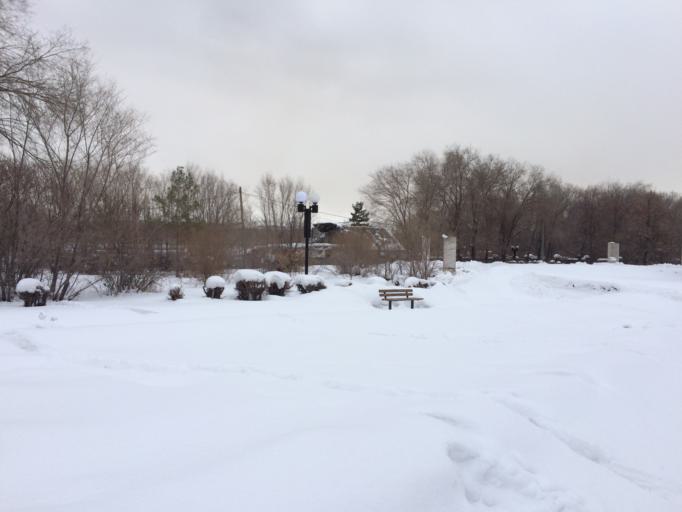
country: RU
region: Chelyabinsk
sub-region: Gorod Magnitogorsk
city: Magnitogorsk
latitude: 53.4161
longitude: 59.0019
